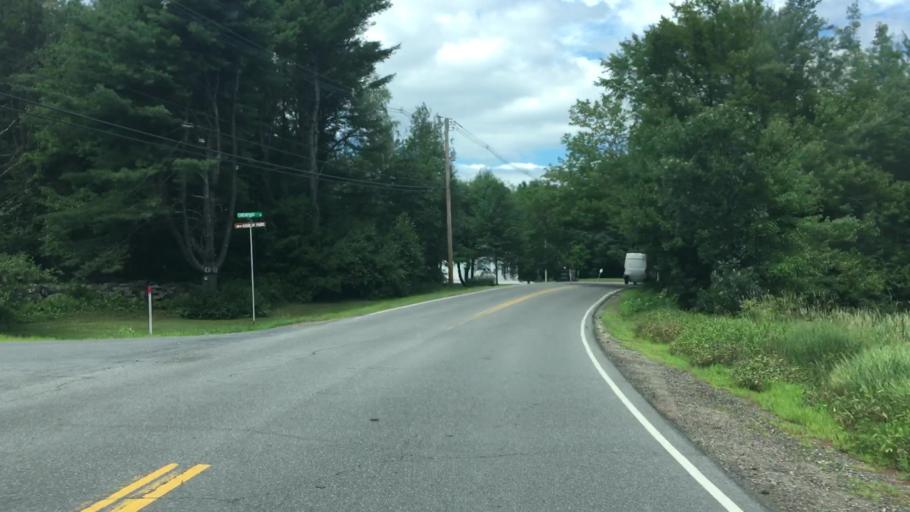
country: US
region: New Hampshire
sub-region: Belknap County
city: Meredith
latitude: 43.6157
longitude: -71.5370
